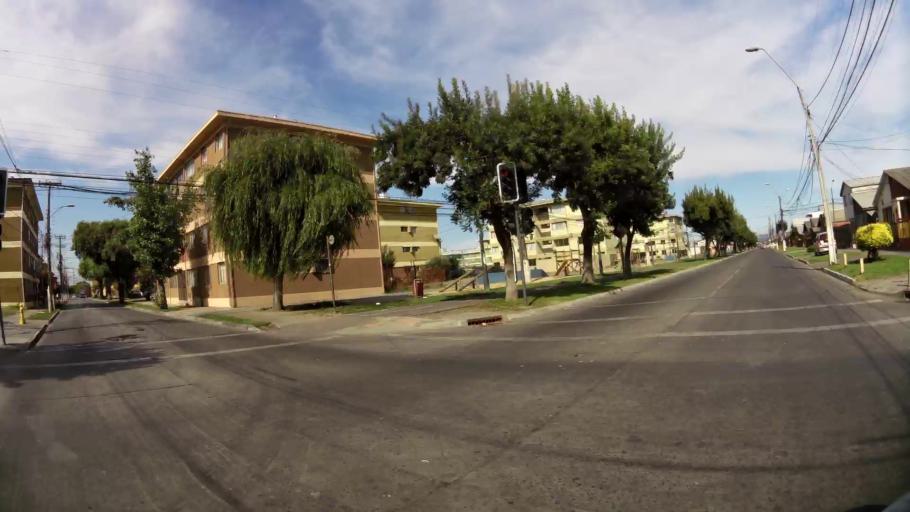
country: CL
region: Biobio
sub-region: Provincia de Concepcion
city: Talcahuano
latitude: -36.7867
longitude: -73.1040
